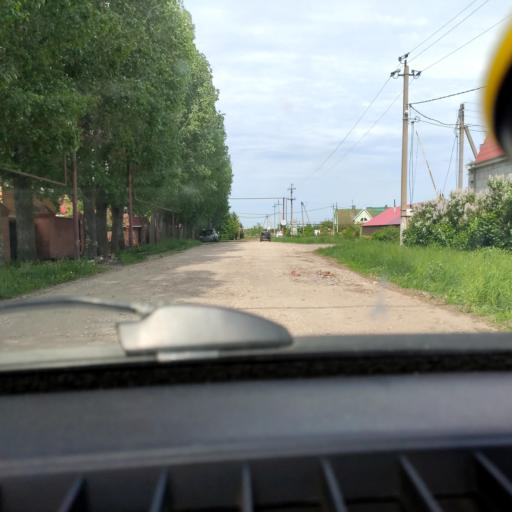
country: RU
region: Samara
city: Povolzhskiy
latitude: 53.5927
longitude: 49.5788
